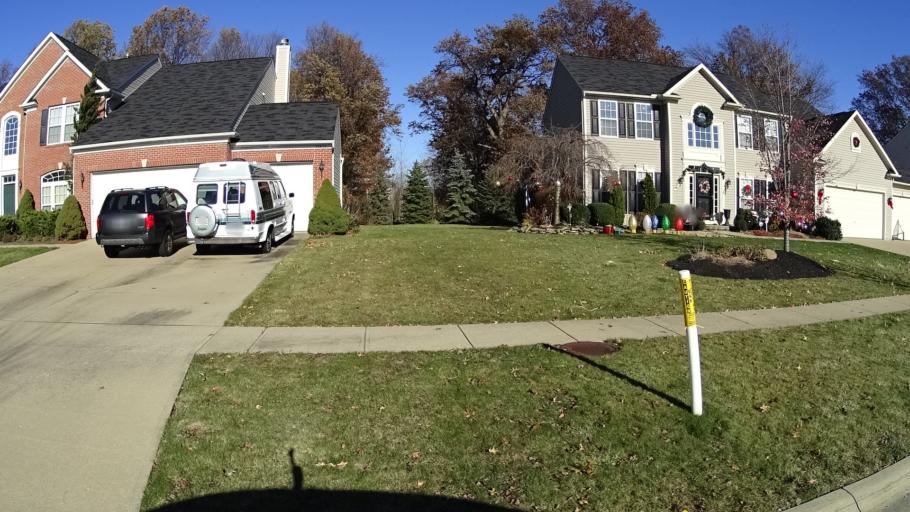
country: US
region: Ohio
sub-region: Lorain County
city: Avon
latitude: 41.4490
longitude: -82.0567
